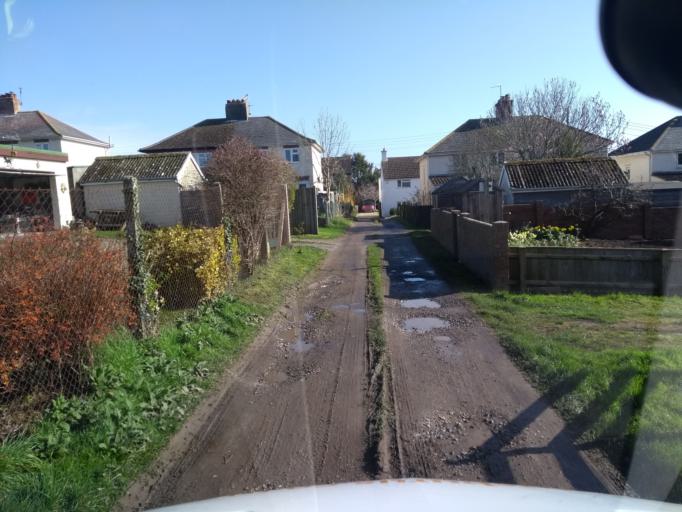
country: GB
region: England
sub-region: Somerset
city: South Petherton
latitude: 50.9538
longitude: -2.8443
